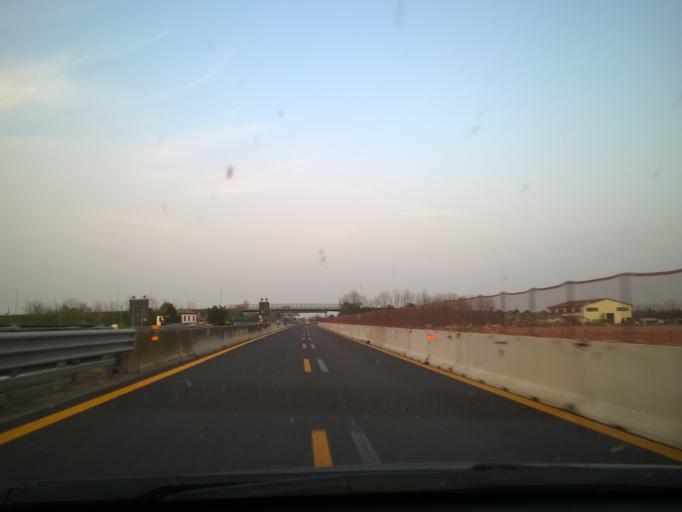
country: IT
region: Veneto
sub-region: Provincia di Padova
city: Masera di Padova
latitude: 45.3391
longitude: 11.8505
